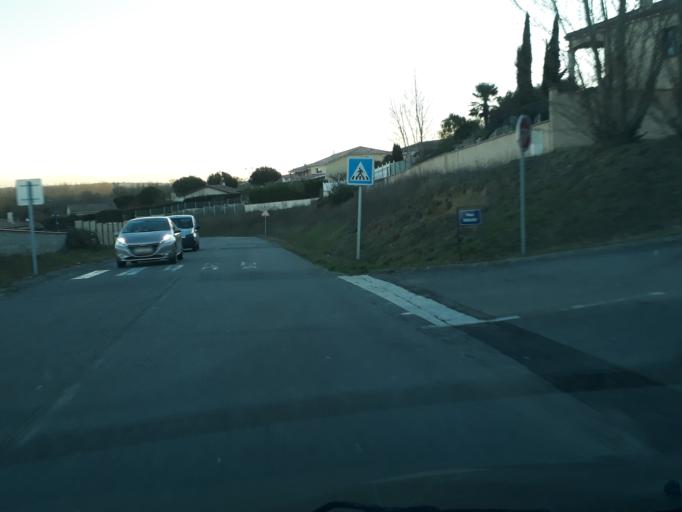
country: FR
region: Midi-Pyrenees
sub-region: Departement du Gers
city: Pujaudran
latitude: 43.6150
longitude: 1.0611
